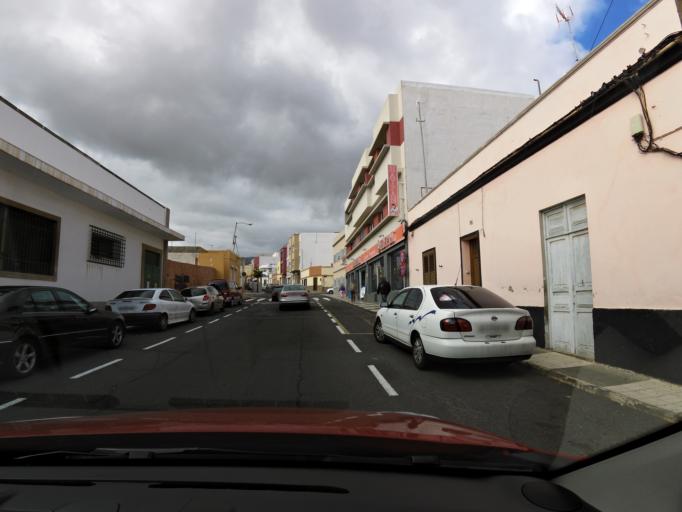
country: ES
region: Canary Islands
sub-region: Provincia de Las Palmas
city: Ingenio
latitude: 27.9188
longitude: -15.4340
